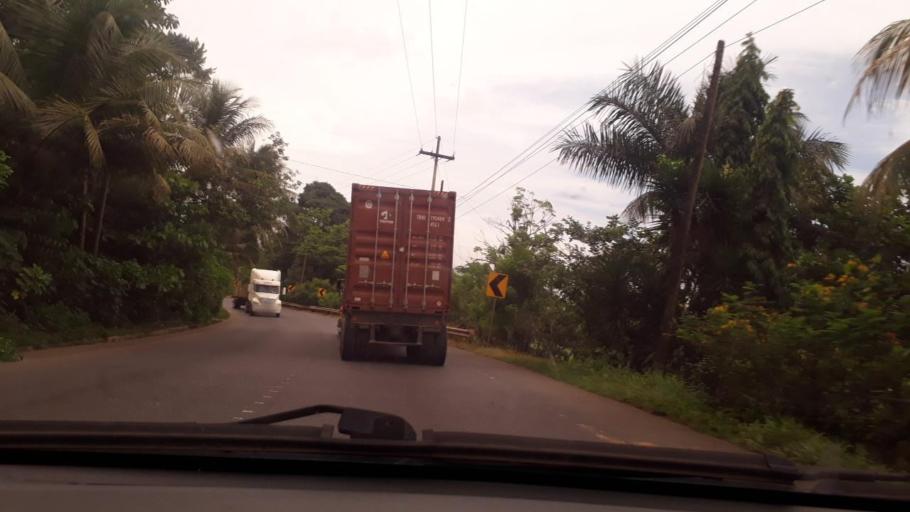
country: GT
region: Izabal
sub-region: Municipio de Puerto Barrios
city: Puerto Barrios
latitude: 15.5994
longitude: -88.5704
